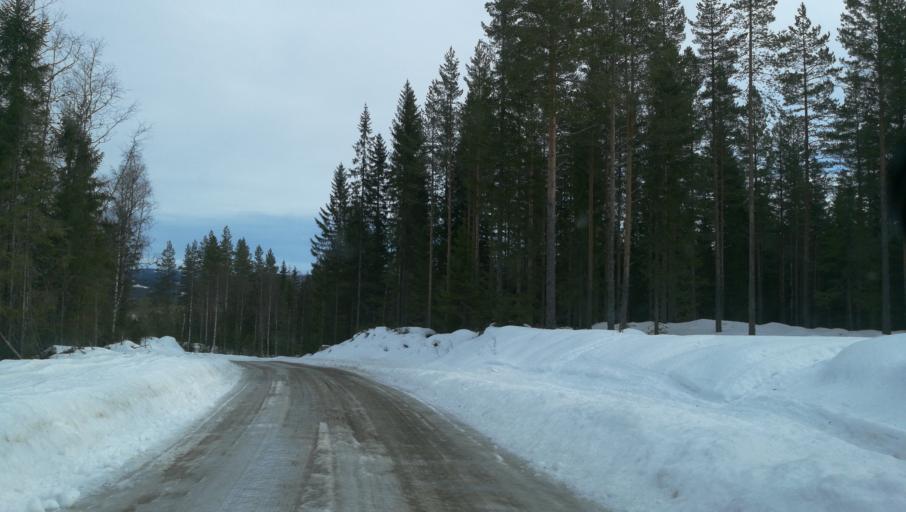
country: SE
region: Vaermland
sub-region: Torsby Kommun
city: Torsby
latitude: 60.6620
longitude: 12.8301
